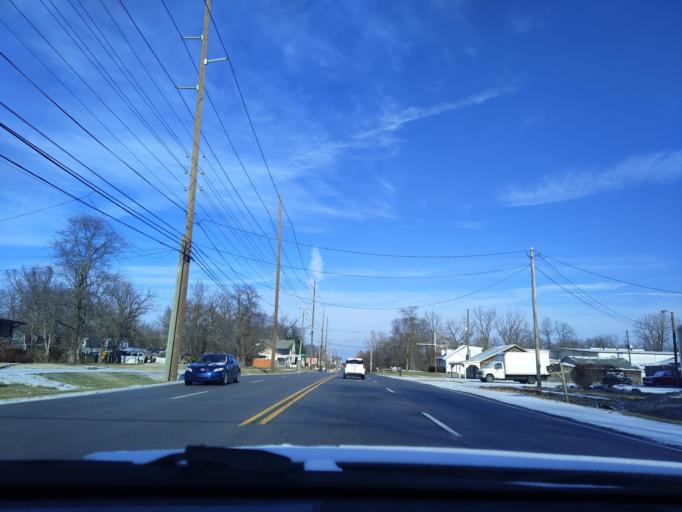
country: US
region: Indiana
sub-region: Marion County
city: Meridian Hills
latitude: 39.8897
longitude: -86.2121
